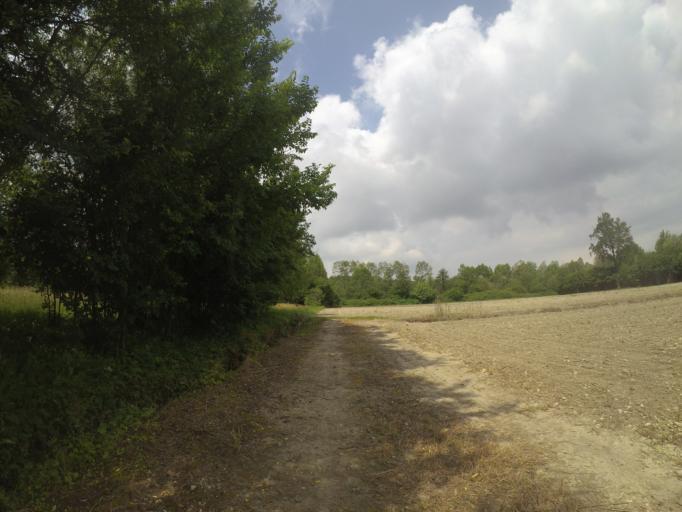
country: IT
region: Friuli Venezia Giulia
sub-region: Provincia di Udine
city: Bertiolo
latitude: 45.9214
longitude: 13.0334
